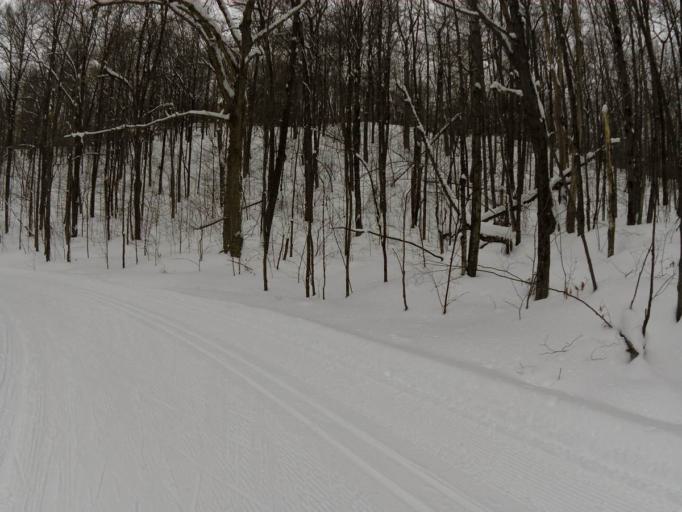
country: CA
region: Quebec
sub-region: Outaouais
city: Wakefield
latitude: 45.5894
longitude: -76.0093
